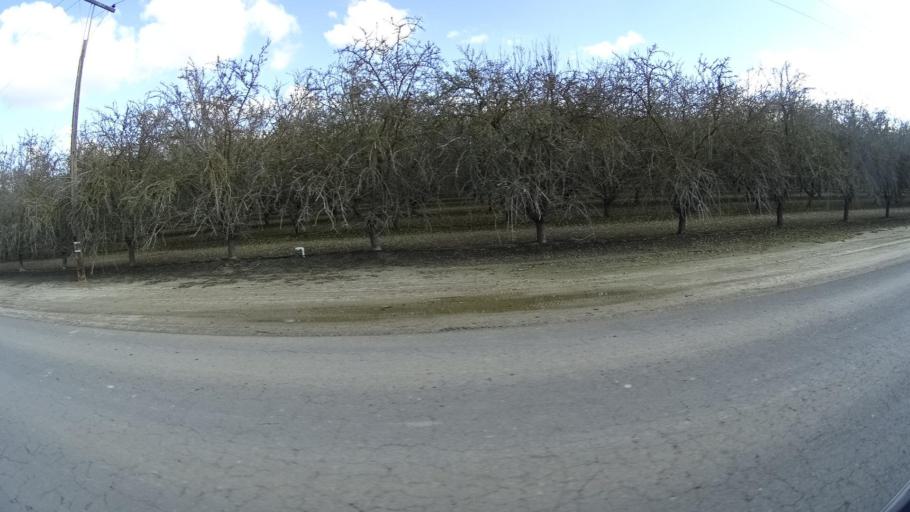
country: US
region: California
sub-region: Kern County
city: Delano
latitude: 35.7277
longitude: -119.3659
